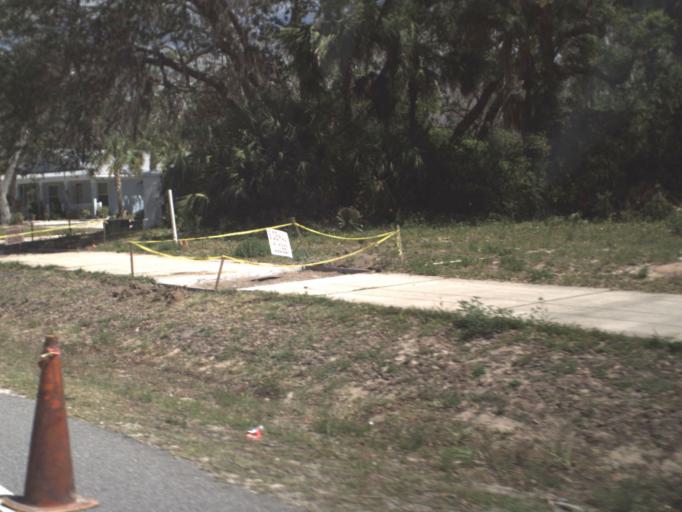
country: US
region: Florida
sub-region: Flagler County
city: Palm Coast
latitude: 29.6253
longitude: -81.2053
